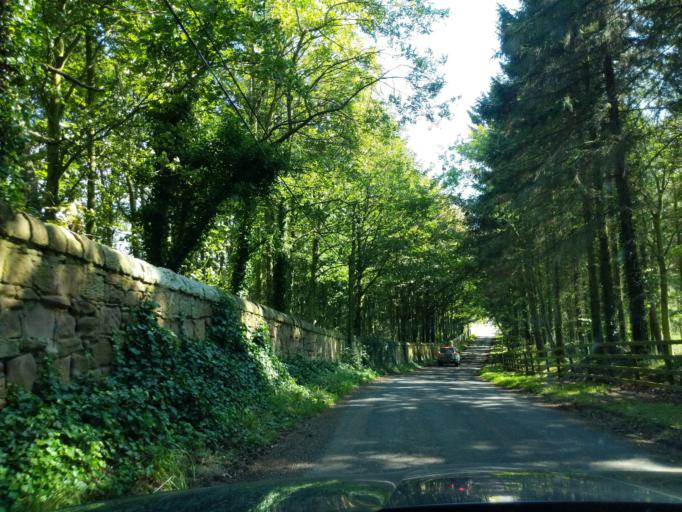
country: GB
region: Scotland
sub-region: The Scottish Borders
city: Coldstream
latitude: 55.6767
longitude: -2.1895
